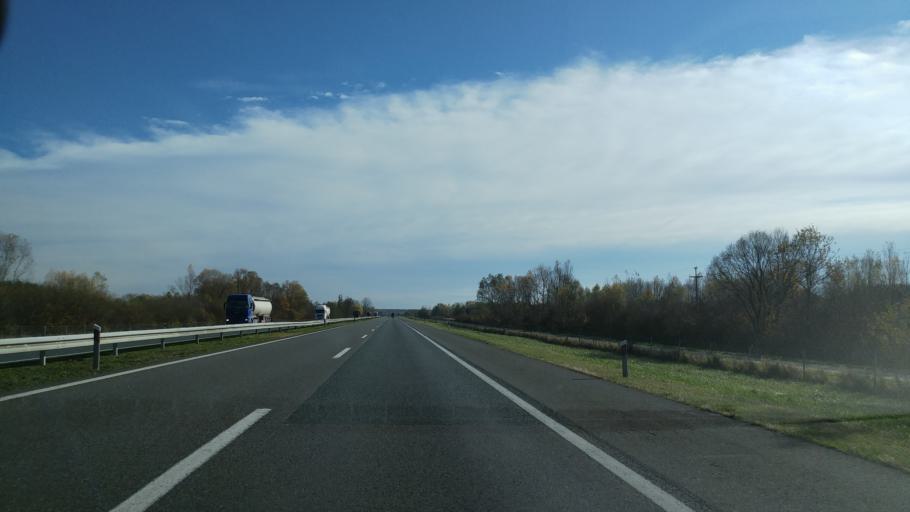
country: HR
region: Brodsko-Posavska
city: Okucani
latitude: 45.2467
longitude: 17.1832
